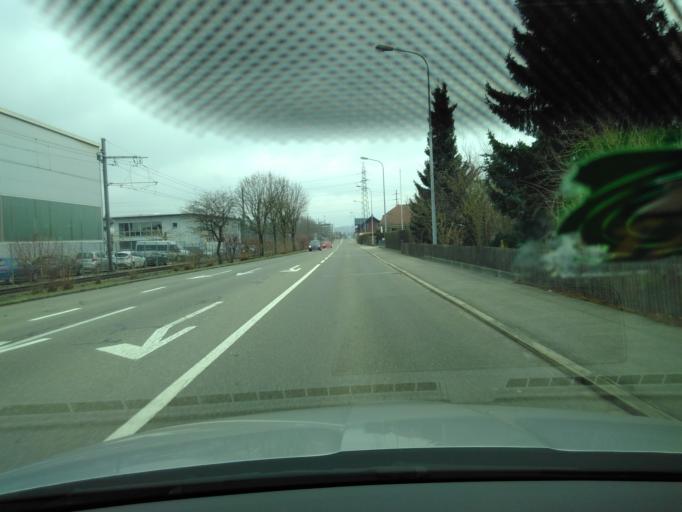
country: CH
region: Aargau
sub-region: Bezirk Aarau
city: Muhen
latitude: 47.3450
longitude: 8.0520
